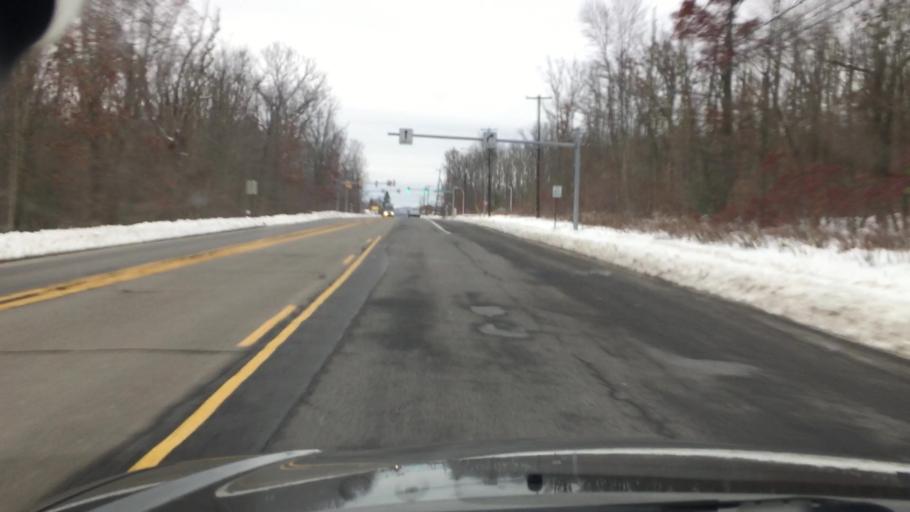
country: US
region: Pennsylvania
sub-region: Luzerne County
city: Mountain Top
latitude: 41.1317
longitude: -75.9050
